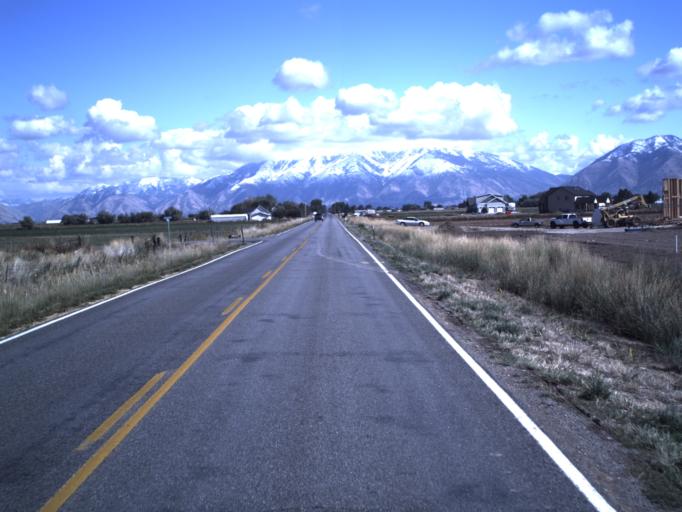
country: US
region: Utah
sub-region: Utah County
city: Benjamin
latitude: 40.0979
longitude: -111.7617
